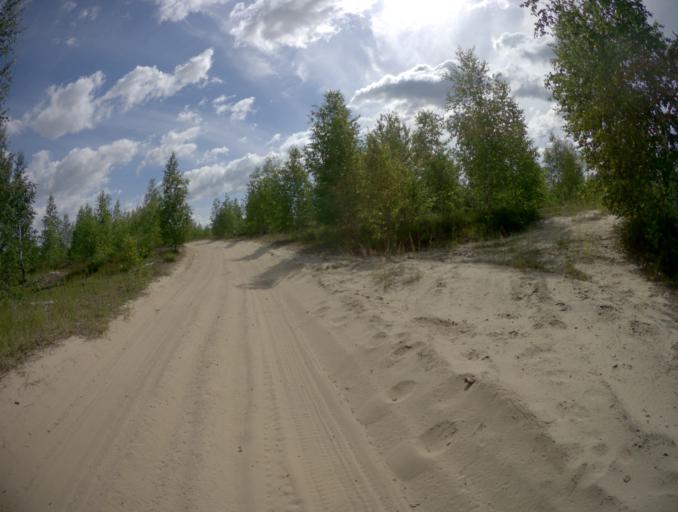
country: RU
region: Ivanovo
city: Talitsy
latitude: 56.5339
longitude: 42.4226
